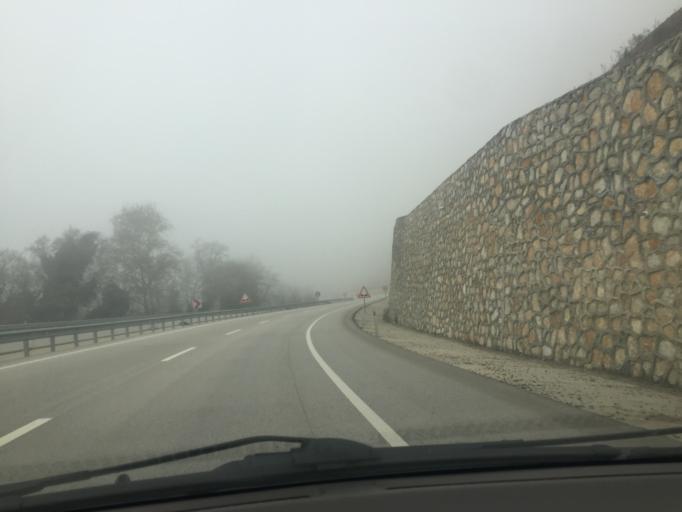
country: TR
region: Canakkale
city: Biga
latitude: 40.1070
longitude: 27.1846
